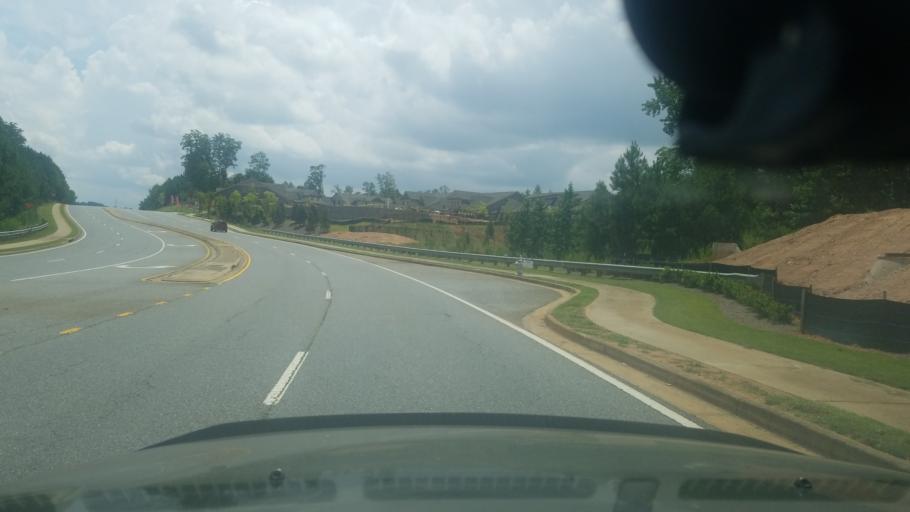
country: US
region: Georgia
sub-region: Fulton County
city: Johns Creek
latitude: 34.0963
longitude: -84.1688
